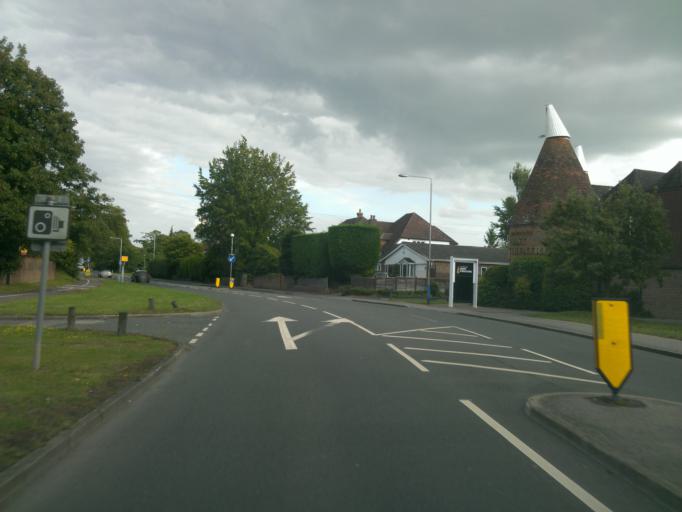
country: GB
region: England
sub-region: Kent
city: Tonbridge
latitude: 51.2064
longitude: 0.2621
